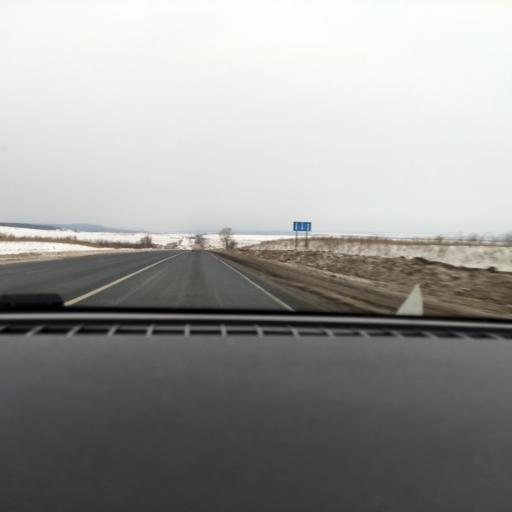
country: RU
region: Samara
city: Novosemeykino
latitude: 53.3987
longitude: 50.4190
